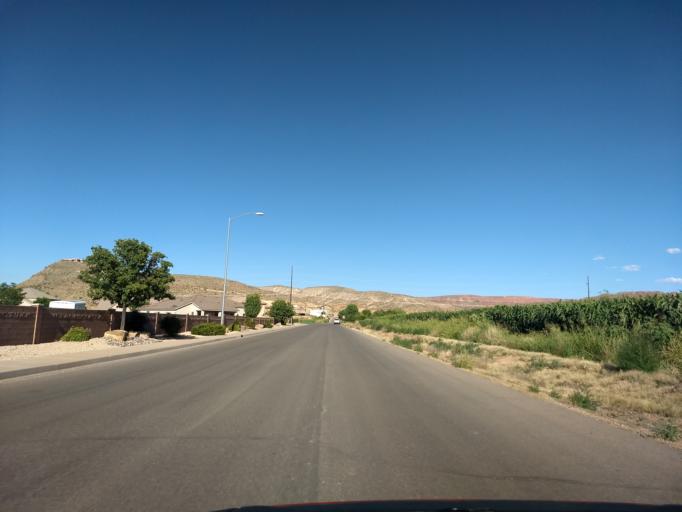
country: US
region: Utah
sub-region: Washington County
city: Washington
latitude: 37.0959
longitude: -113.5112
